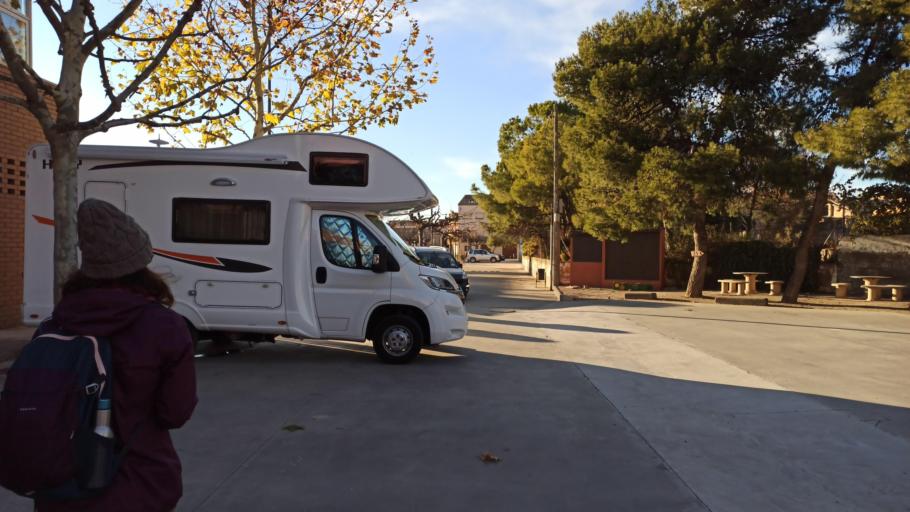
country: ES
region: Catalonia
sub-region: Provincia de Lleida
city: Penelles
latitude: 41.7577
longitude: 0.9673
